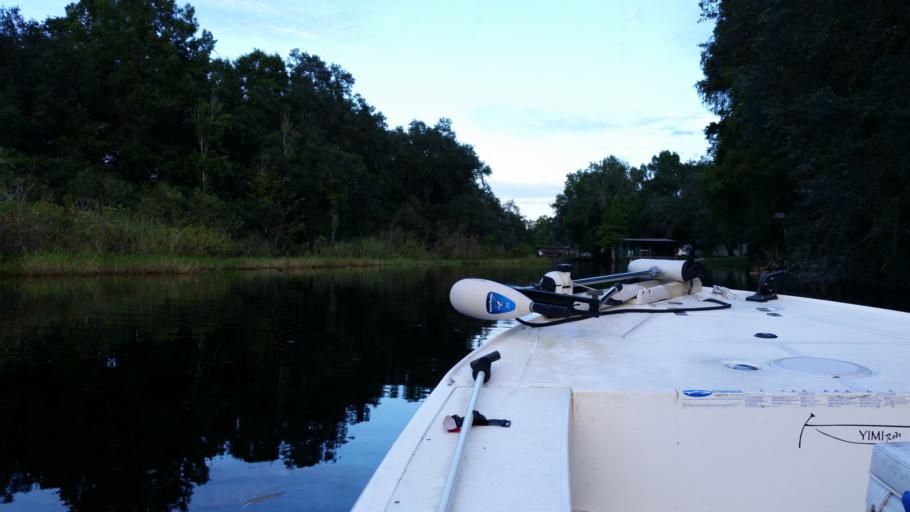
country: US
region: Florida
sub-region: Citrus County
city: Inverness
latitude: 28.8306
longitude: -82.2906
